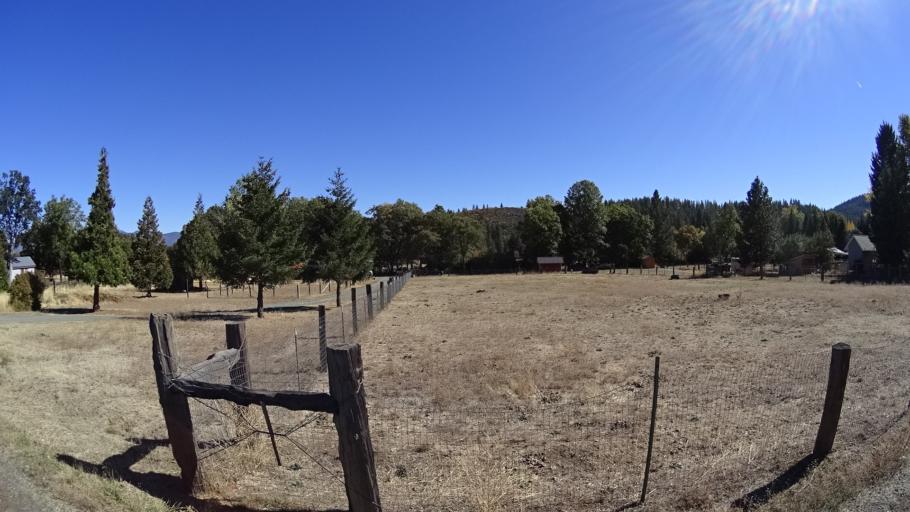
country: US
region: California
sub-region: Siskiyou County
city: Yreka
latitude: 41.4513
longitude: -122.8991
